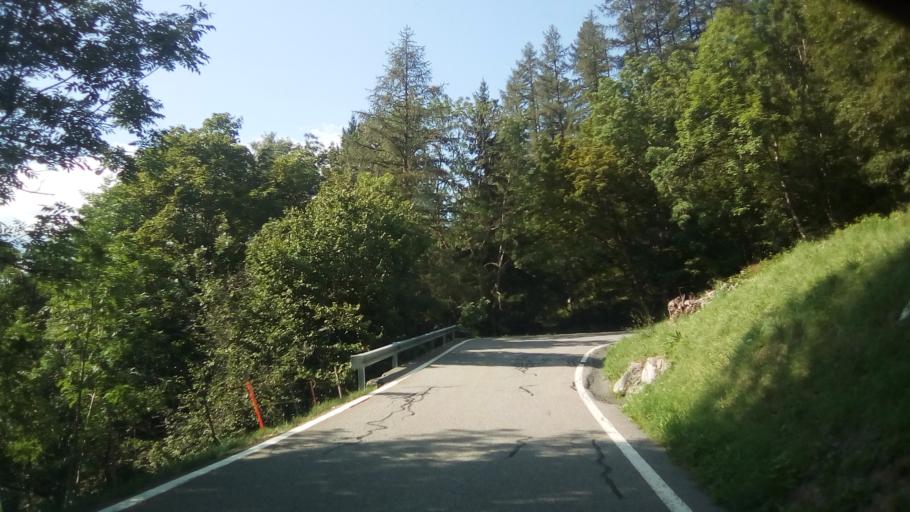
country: CH
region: Valais
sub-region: Martigny District
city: Martigny-Combe
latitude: 46.0545
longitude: 7.0823
